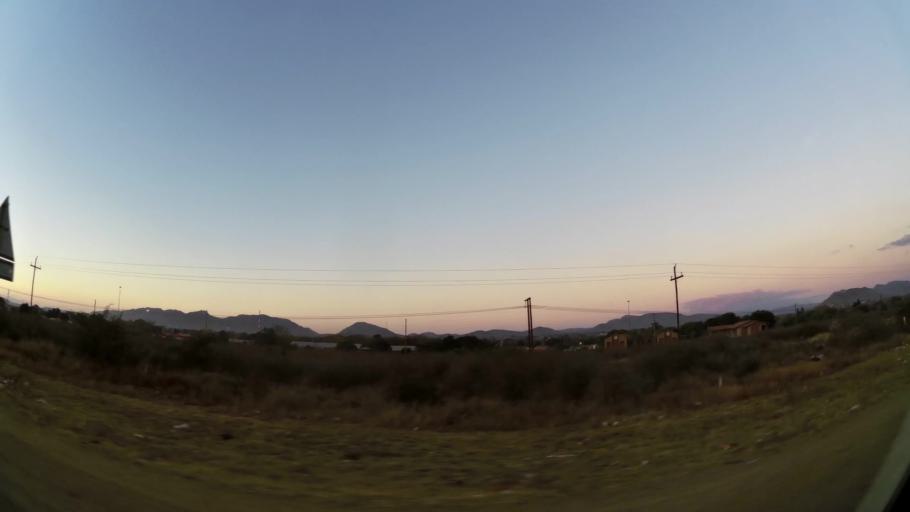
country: ZA
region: Limpopo
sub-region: Waterberg District Municipality
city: Mokopane
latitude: -24.1530
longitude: 28.9764
